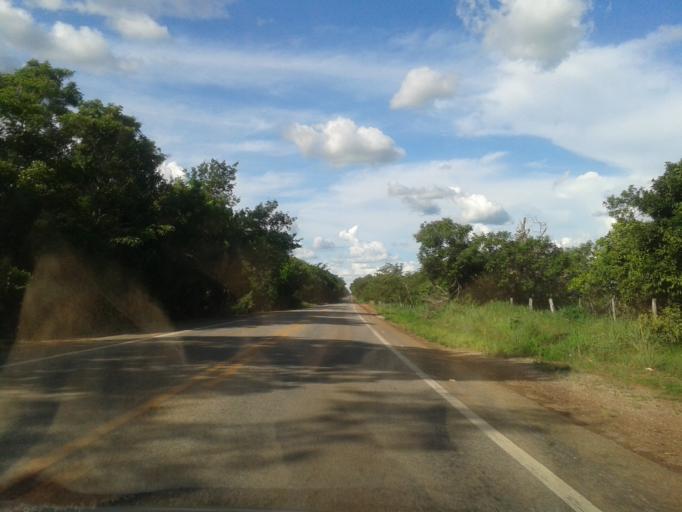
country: BR
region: Goias
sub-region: Mozarlandia
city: Mozarlandia
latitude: -14.6967
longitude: -50.5453
